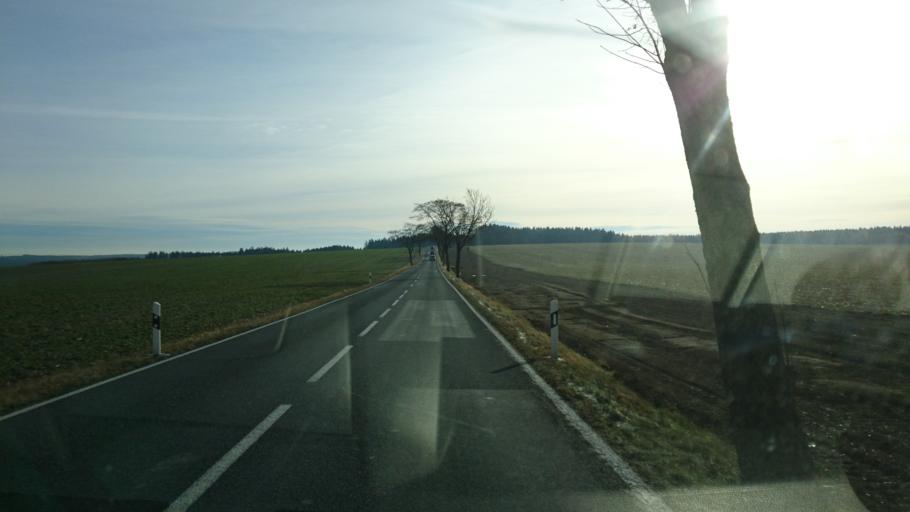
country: DE
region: Thuringia
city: Tanna
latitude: 50.5288
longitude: 11.8755
